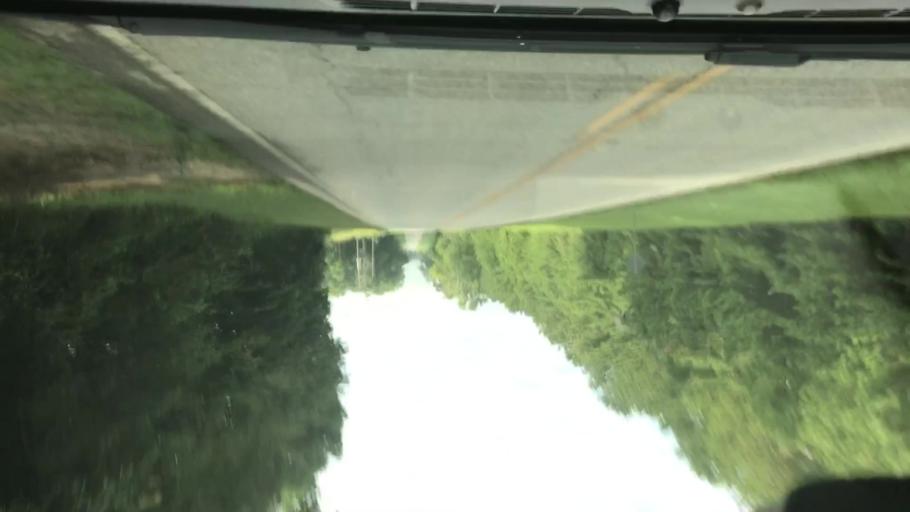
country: US
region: Georgia
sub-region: Quitman County
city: Georgetown
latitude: 31.7734
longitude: -85.0919
